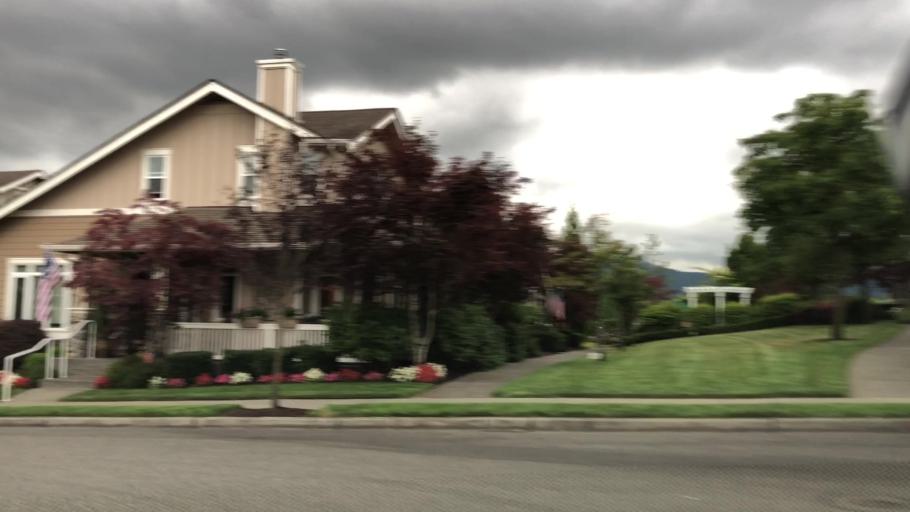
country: US
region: Washington
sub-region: King County
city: Fall City
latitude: 47.5342
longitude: -121.8704
